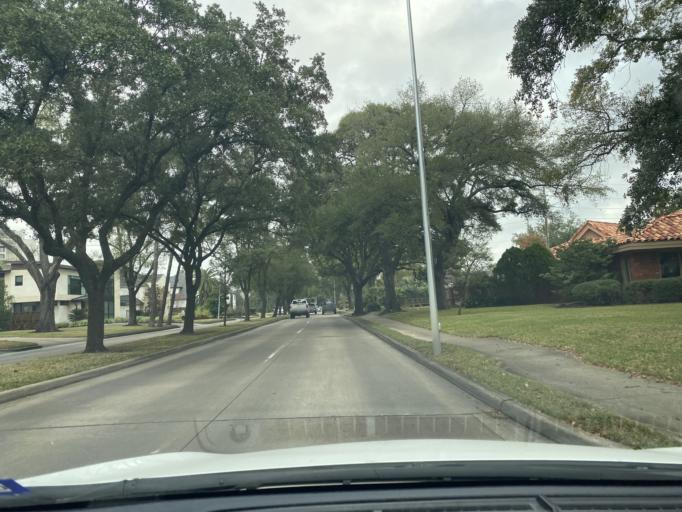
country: US
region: Texas
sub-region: Harris County
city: Hunters Creek Village
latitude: 29.7524
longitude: -95.4772
